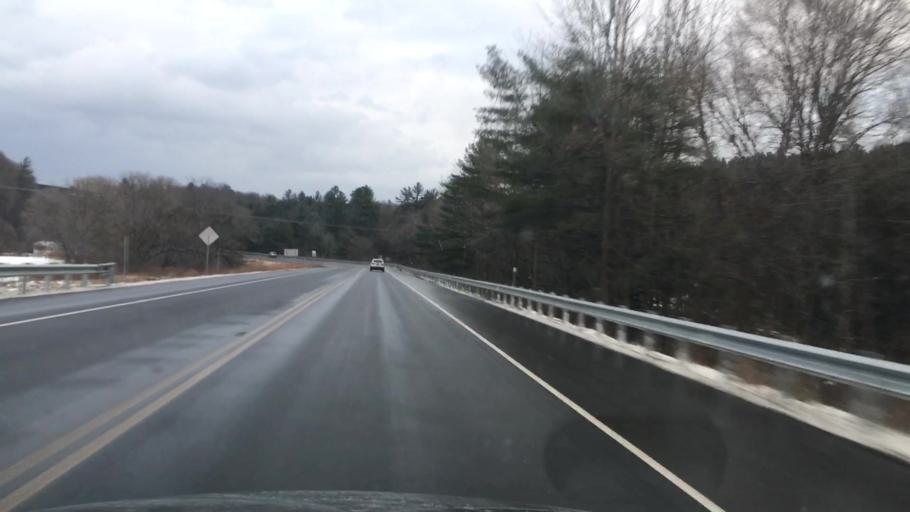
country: US
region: New Hampshire
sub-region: Sullivan County
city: Claremont
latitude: 43.3972
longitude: -72.3917
